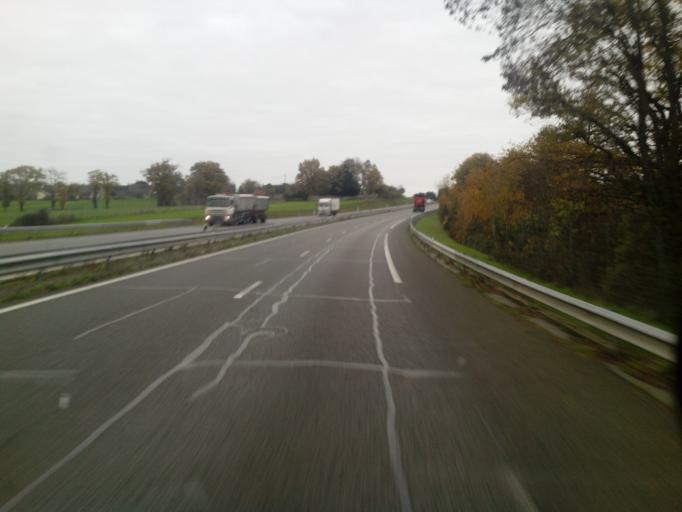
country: FR
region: Brittany
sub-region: Departement d'Ille-et-Vilaine
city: Bain-de-Bretagne
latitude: 47.8720
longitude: -1.6891
